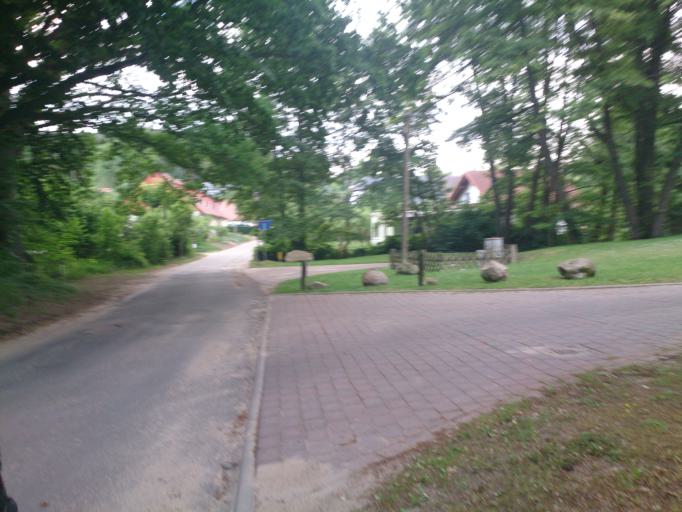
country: DE
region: Mecklenburg-Vorpommern
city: Plau am See
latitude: 53.4319
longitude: 12.3156
